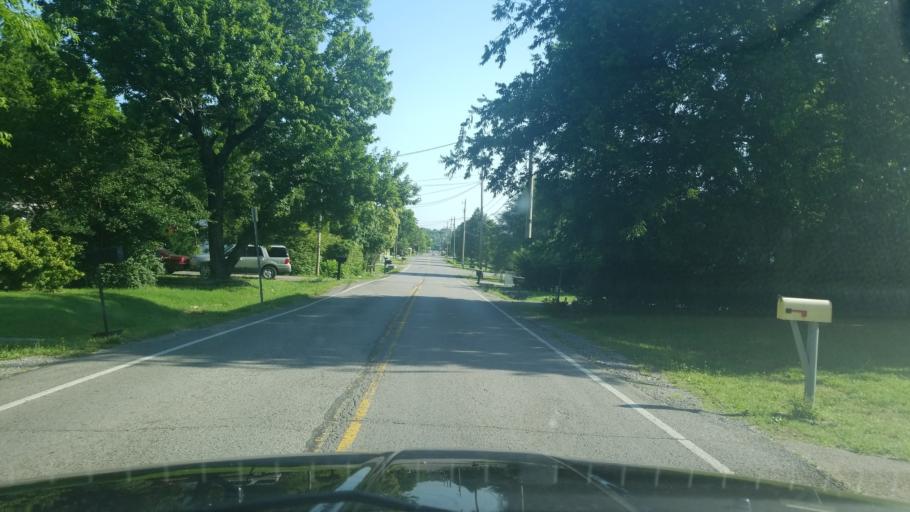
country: US
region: Tennessee
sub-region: Davidson County
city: Oak Hill
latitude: 36.1068
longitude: -86.7476
